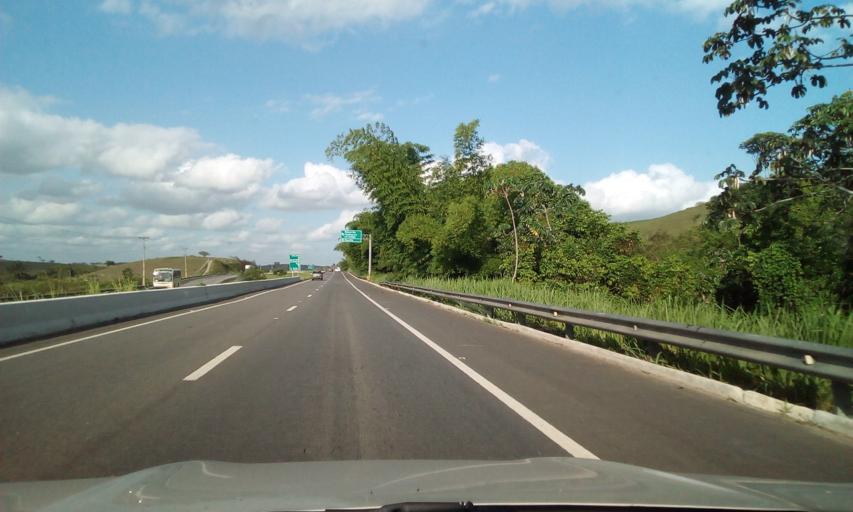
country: BR
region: Pernambuco
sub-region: Ribeirao
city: Ribeirao
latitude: -8.4557
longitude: -35.3598
